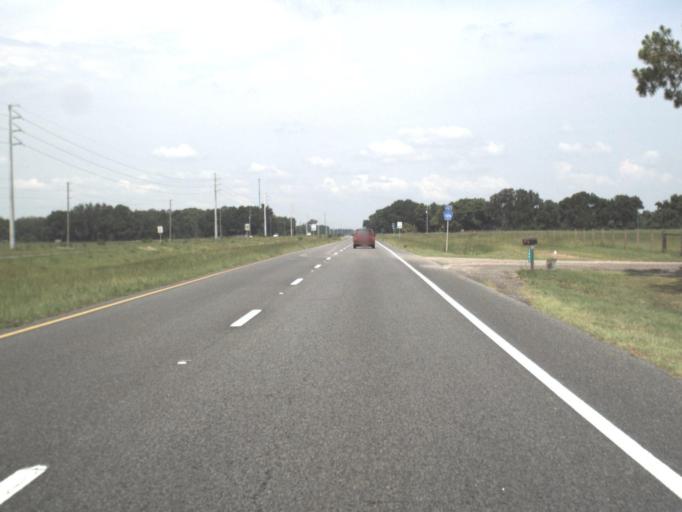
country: US
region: Florida
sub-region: Levy County
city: Chiefland
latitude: 29.4752
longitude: -82.7517
